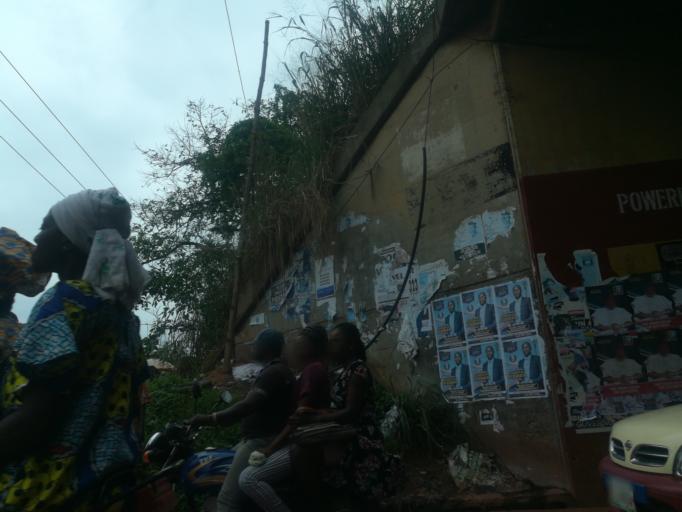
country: NG
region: Oyo
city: Ibadan
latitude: 7.3915
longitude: 3.9357
